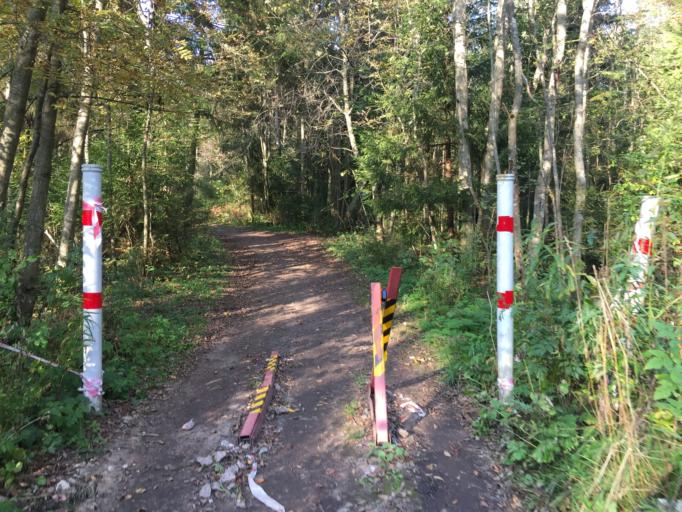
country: RU
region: Leningrad
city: Toksovo
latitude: 60.1313
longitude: 30.4446
